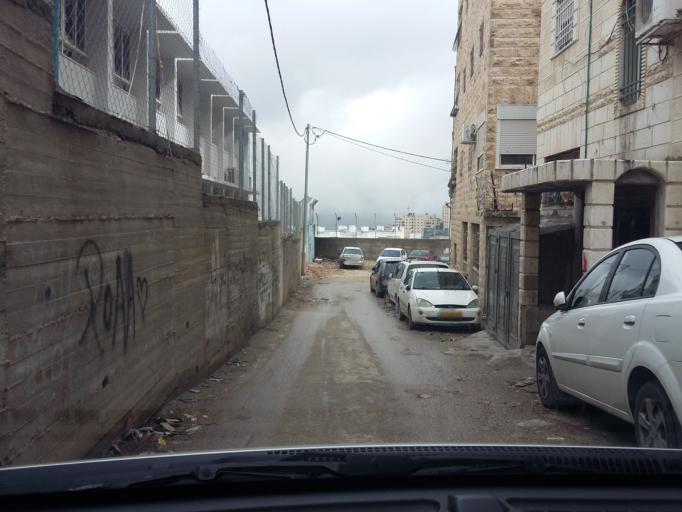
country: PS
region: West Bank
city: `Anata
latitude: 31.8101
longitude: 35.2447
